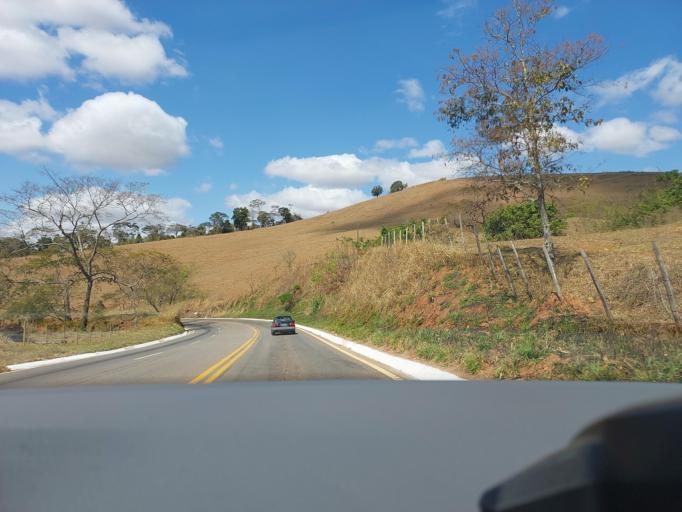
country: BR
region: Minas Gerais
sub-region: Muriae
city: Muriae
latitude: -21.0911
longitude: -42.4818
